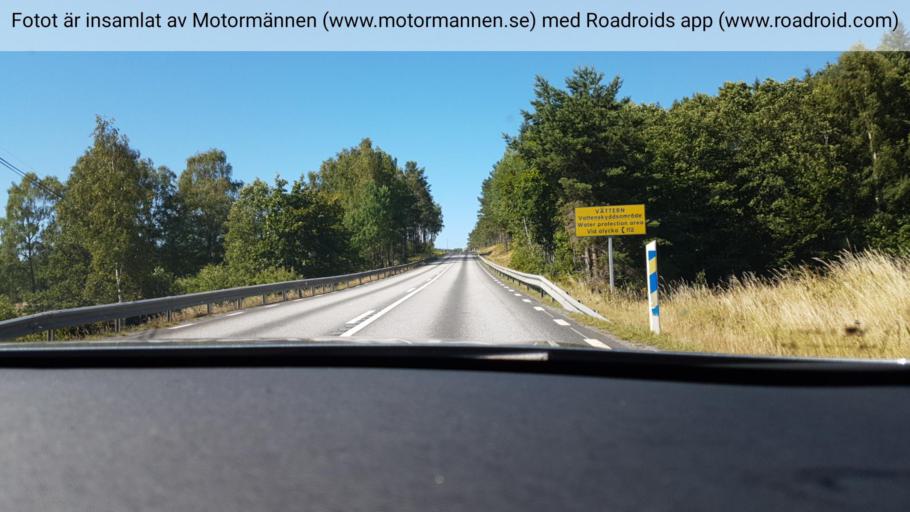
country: SE
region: Joenkoeping
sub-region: Habo Kommun
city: Habo
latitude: 58.0291
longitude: 14.1650
